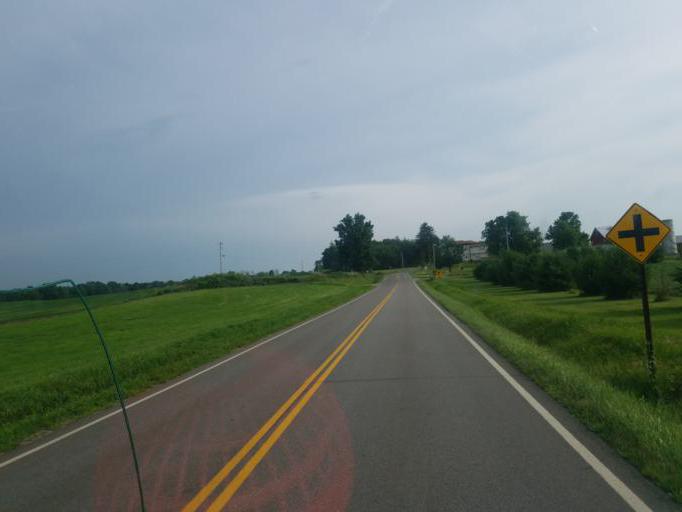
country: US
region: Ohio
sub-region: Ashland County
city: Ashland
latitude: 40.7560
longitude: -82.2688
